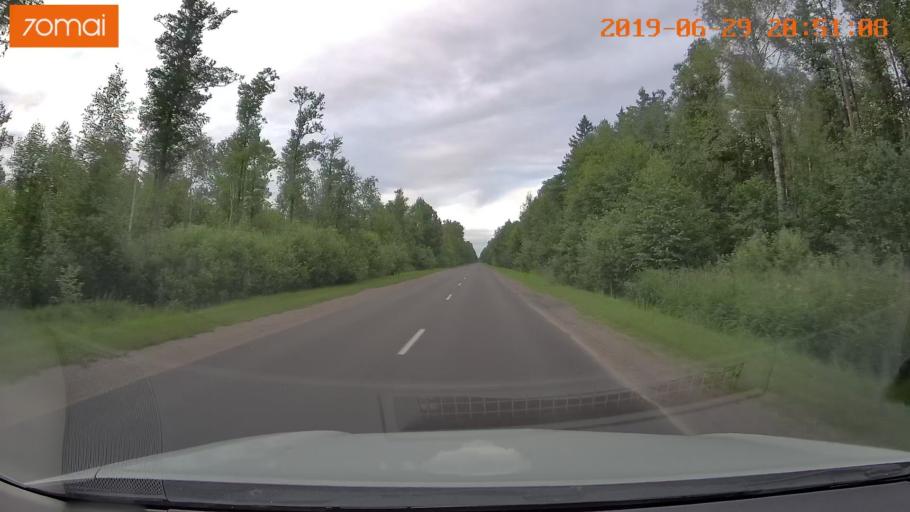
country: BY
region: Brest
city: Hantsavichy
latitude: 52.6846
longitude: 26.3454
